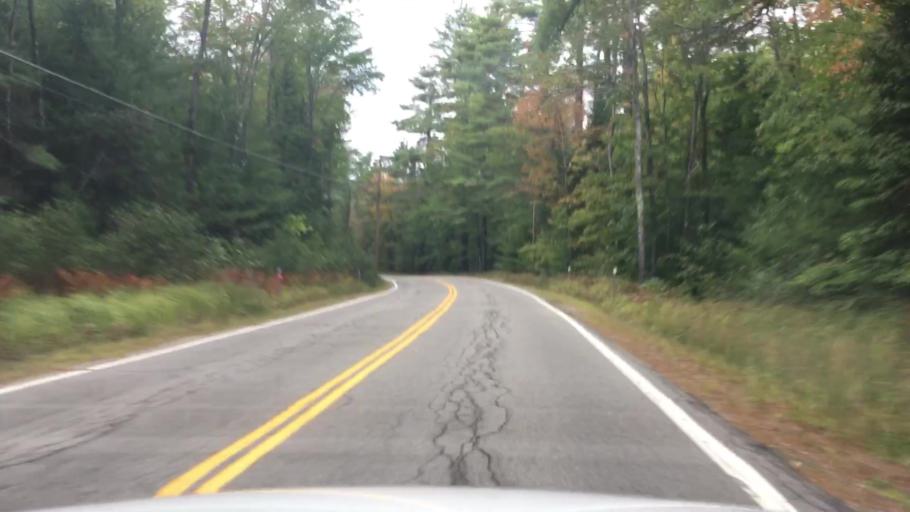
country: US
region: New Hampshire
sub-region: Carroll County
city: Effingham
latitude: 43.7311
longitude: -71.0039
